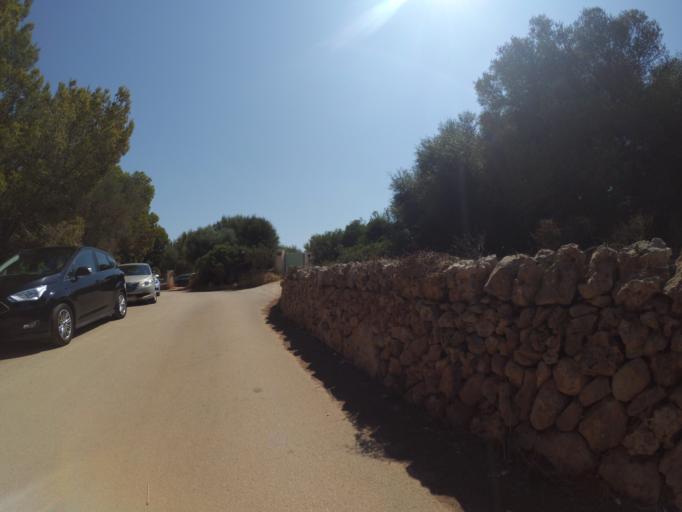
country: ES
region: Balearic Islands
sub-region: Illes Balears
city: Santanyi
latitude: 39.3928
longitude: 3.2460
